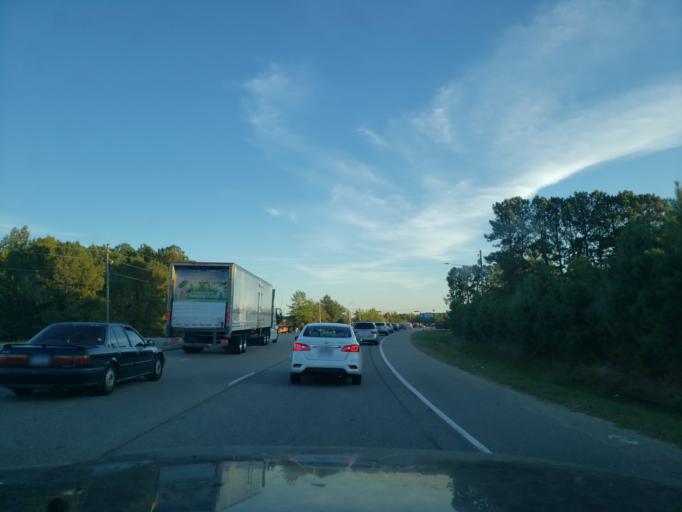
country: US
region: North Carolina
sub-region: Wake County
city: Morrisville
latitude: 35.8246
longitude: -78.8489
